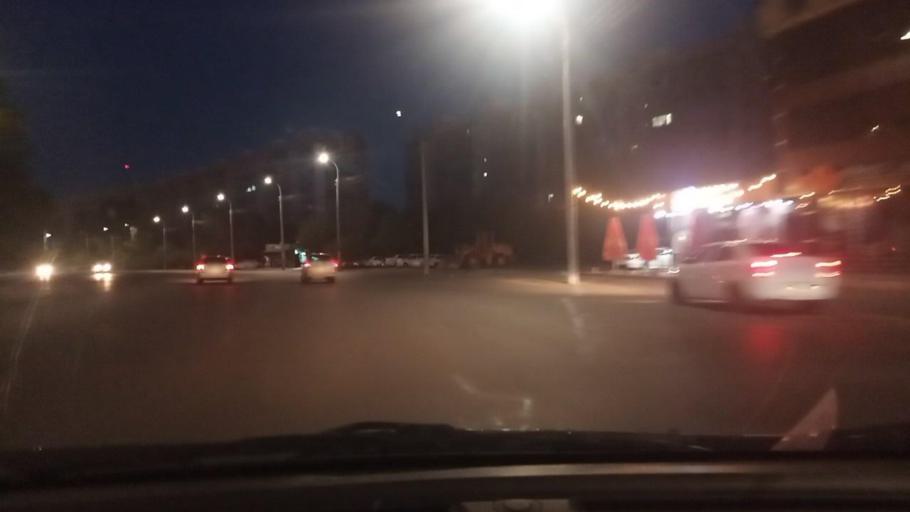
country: UZ
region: Toshkent Shahri
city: Tashkent
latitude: 41.2696
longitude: 69.2567
